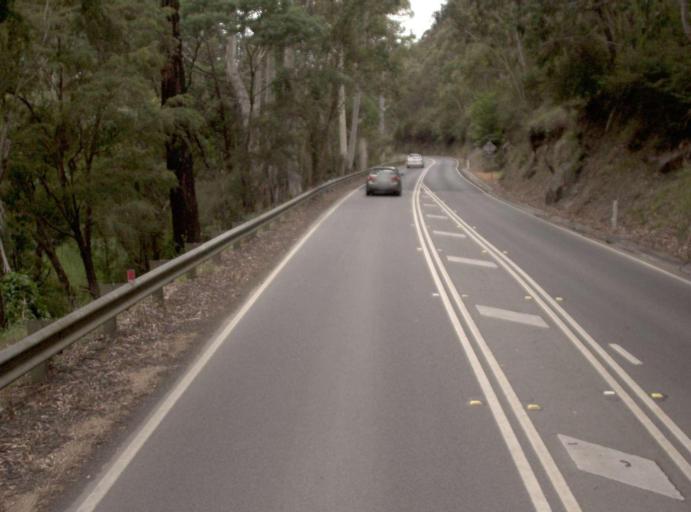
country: AU
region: Victoria
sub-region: Yarra Ranges
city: Millgrove
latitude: -37.7533
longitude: 145.6579
